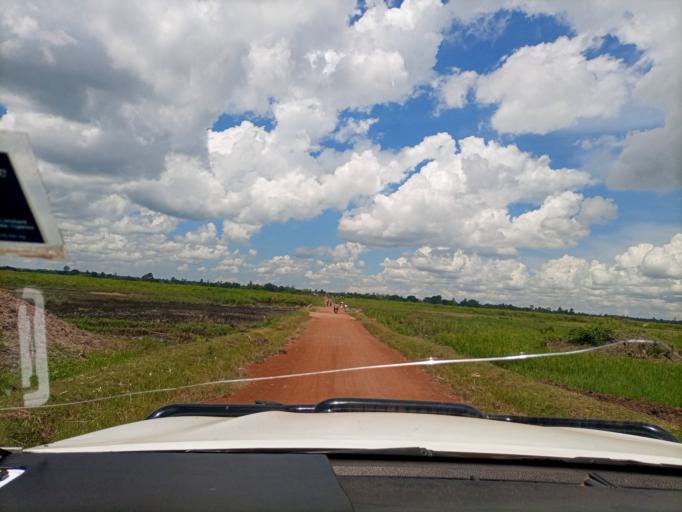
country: UG
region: Eastern Region
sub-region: Tororo District
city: Tororo
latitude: 0.6409
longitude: 33.9942
